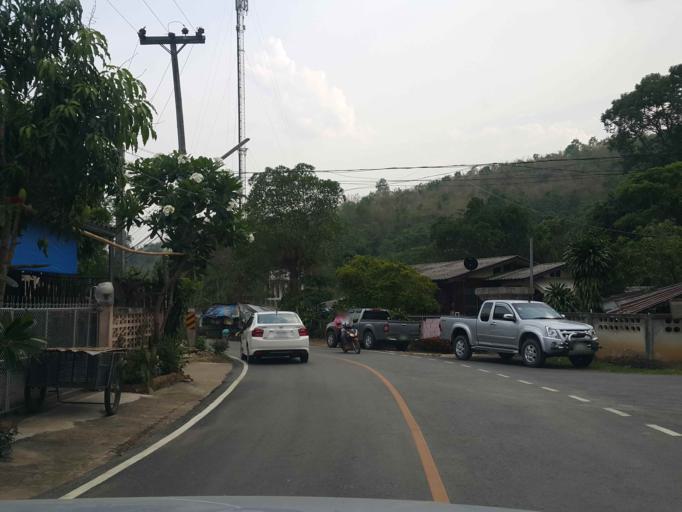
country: TH
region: Chiang Mai
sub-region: Amphoe Chiang Dao
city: Chiang Dao
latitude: 19.3926
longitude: 98.9299
